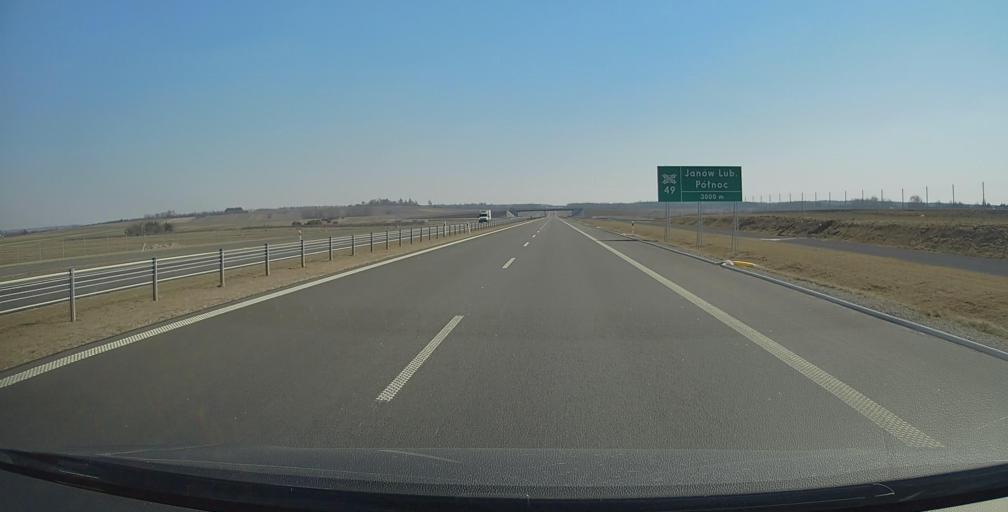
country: PL
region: Lublin Voivodeship
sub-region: Powiat janowski
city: Modliborzyce
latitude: 50.7426
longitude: 22.3088
